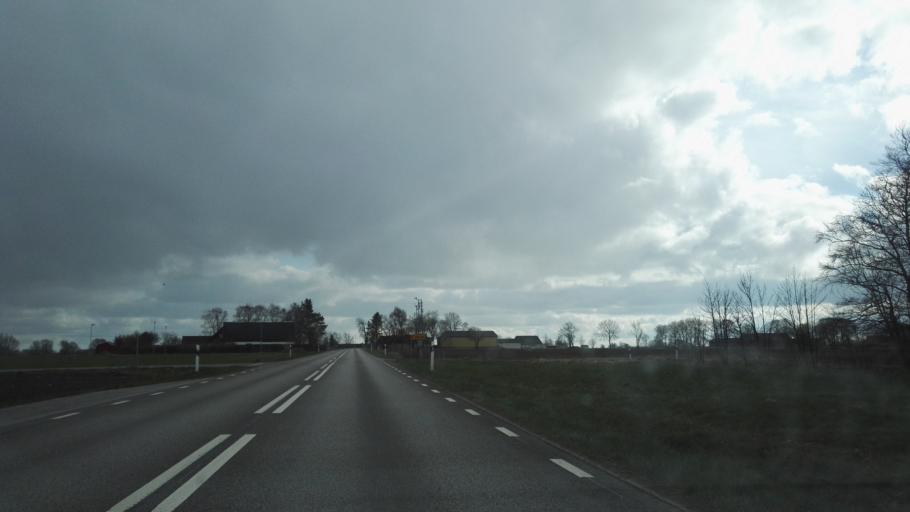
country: SE
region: Skane
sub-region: Horby Kommun
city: Hoerby
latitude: 55.7803
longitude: 13.6757
